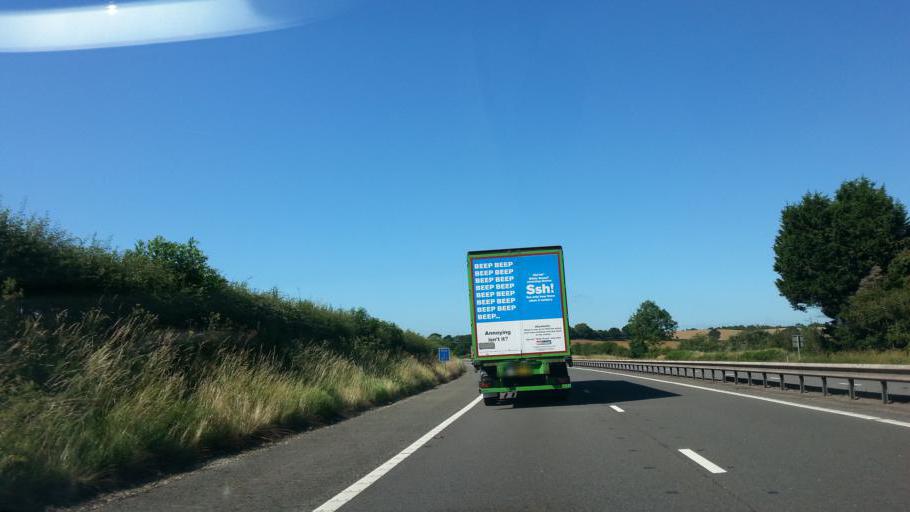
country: GB
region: England
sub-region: Herefordshire
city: Donnington
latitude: 51.9924
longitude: -2.3929
